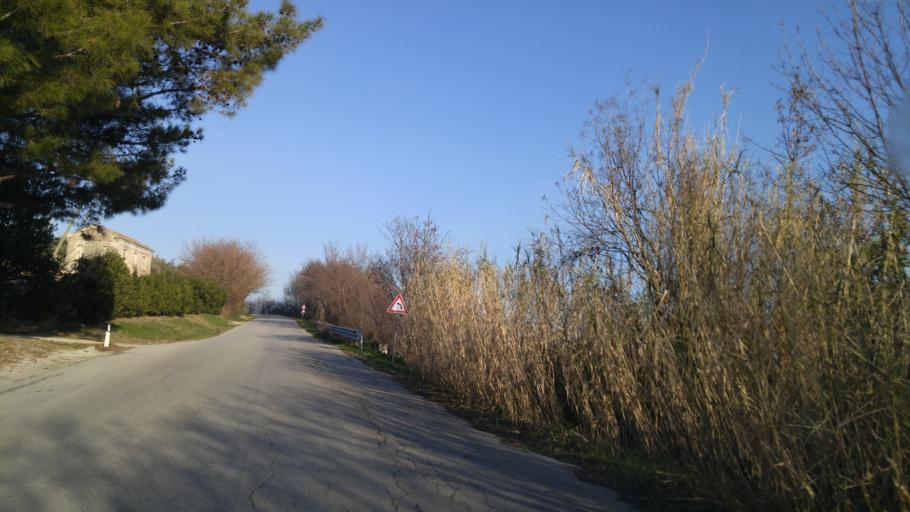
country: IT
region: The Marches
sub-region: Provincia di Pesaro e Urbino
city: Montemaggiore al Metauro
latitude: 43.7385
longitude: 12.9542
